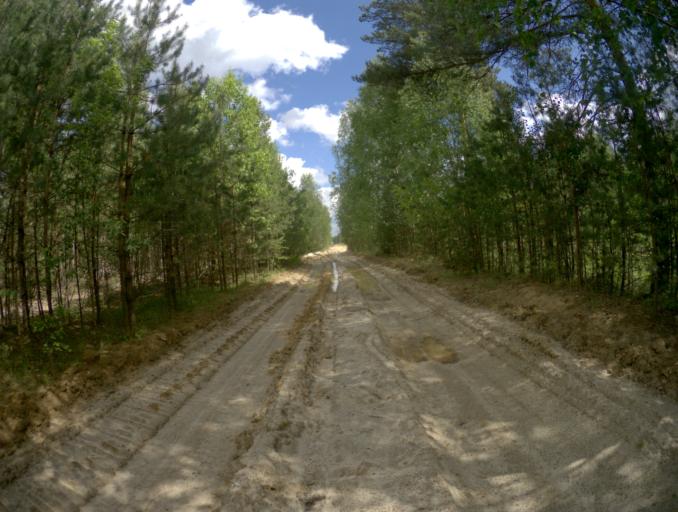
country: RU
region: Vladimir
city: Velikodvorskiy
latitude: 55.2264
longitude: 40.6374
